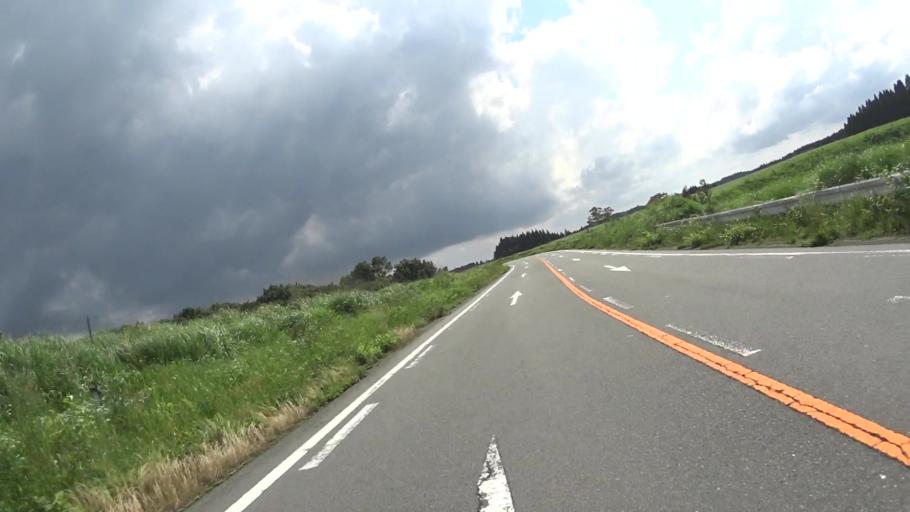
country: JP
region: Kumamoto
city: Aso
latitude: 33.0324
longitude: 131.1641
